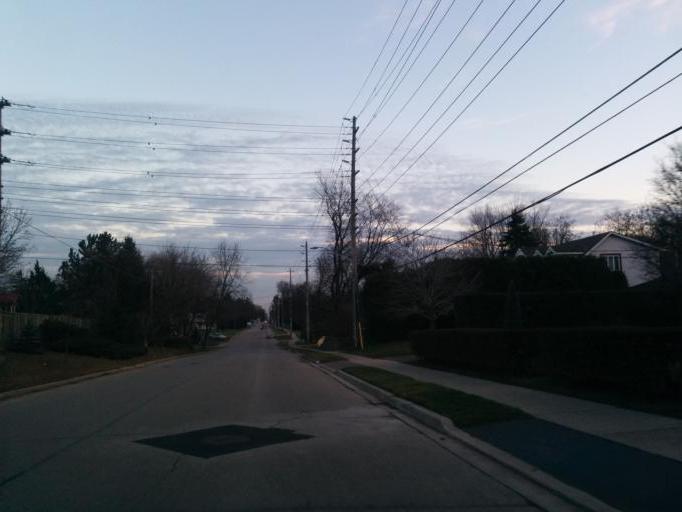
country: CA
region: Ontario
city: Etobicoke
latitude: 43.5913
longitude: -79.5716
